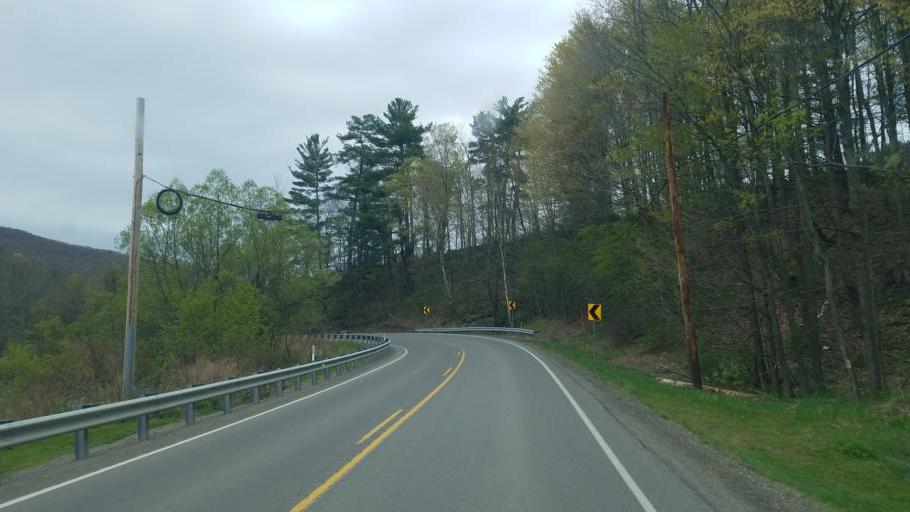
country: US
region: Pennsylvania
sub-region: Tioga County
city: Westfield
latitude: 41.9678
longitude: -77.4520
